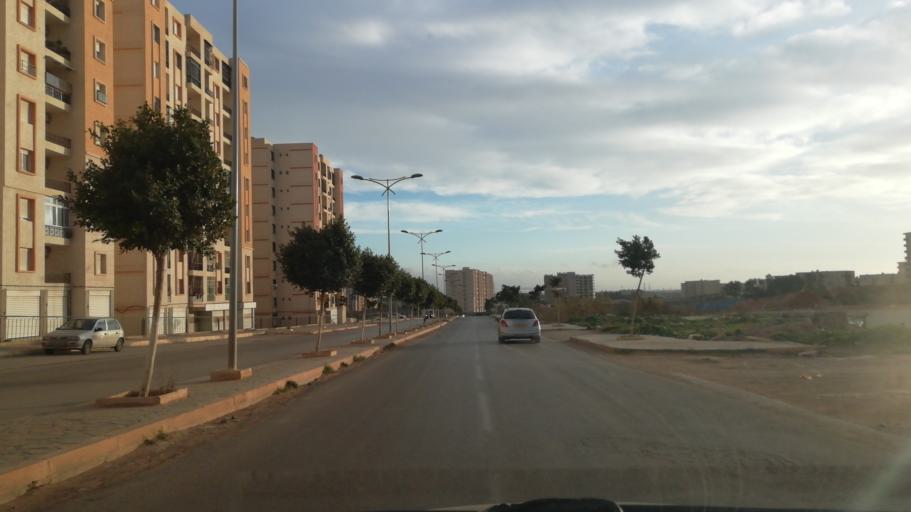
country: DZ
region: Oran
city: Bir el Djir
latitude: 35.6920
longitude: -0.5860
